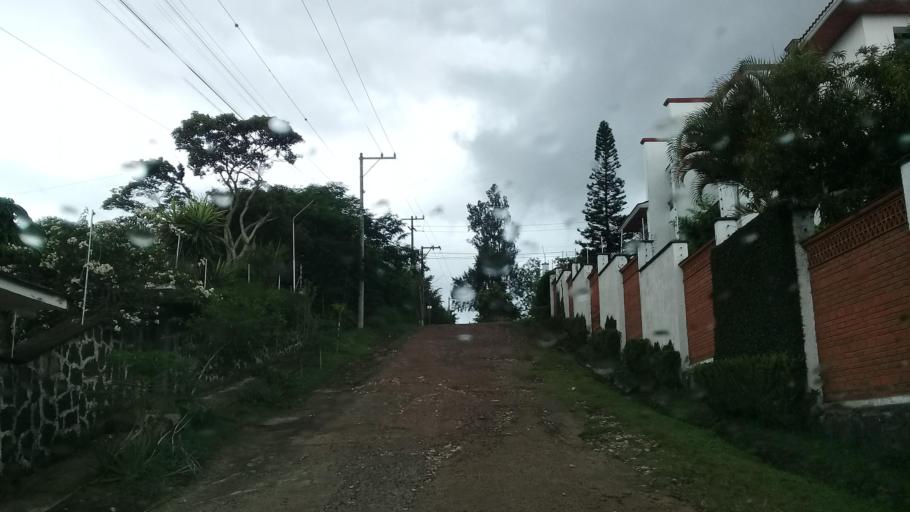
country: MX
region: Veracruz
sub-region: Emiliano Zapata
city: Jacarandas
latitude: 19.5066
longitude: -96.8496
